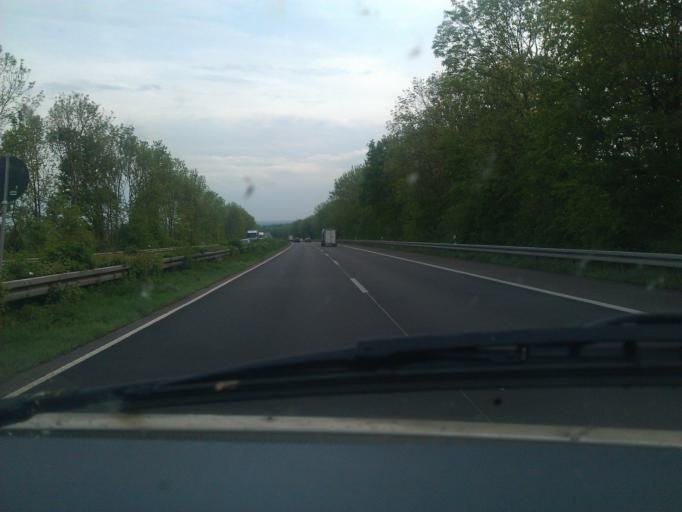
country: DE
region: North Rhine-Westphalia
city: Julich
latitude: 50.9511
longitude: 6.3498
